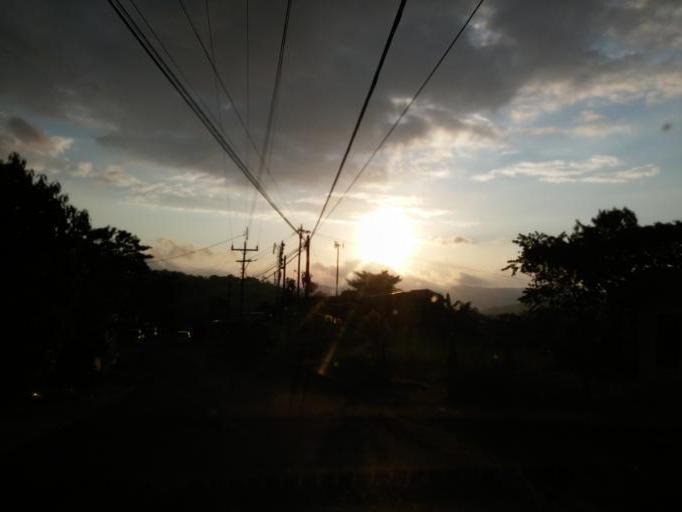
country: CR
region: San Jose
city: Palmichal
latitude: 9.8485
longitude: -84.2319
